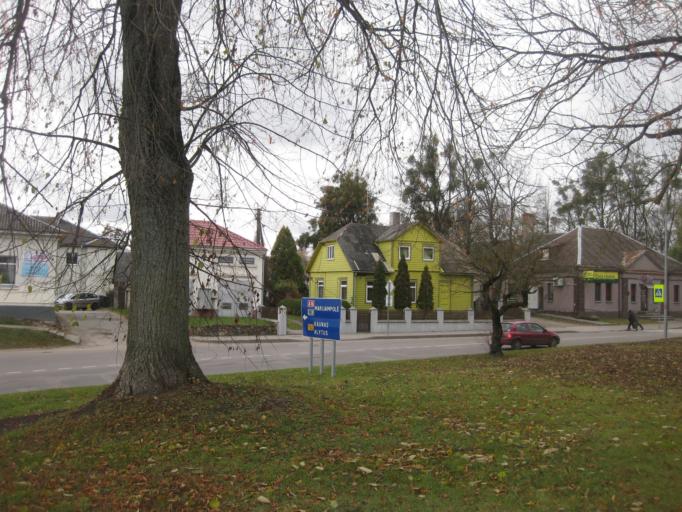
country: LT
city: Prienai
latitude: 54.6318
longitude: 23.9490
